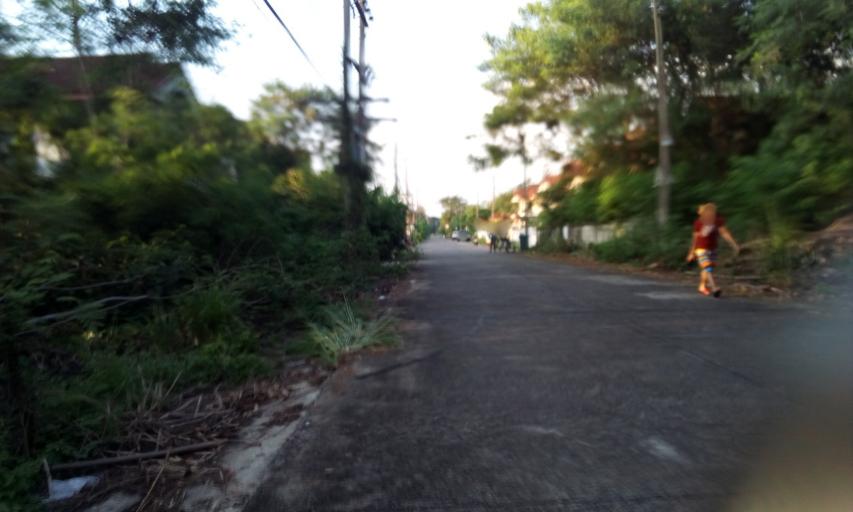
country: TH
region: Pathum Thani
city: Ban Rangsit
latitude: 14.0472
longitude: 100.8223
